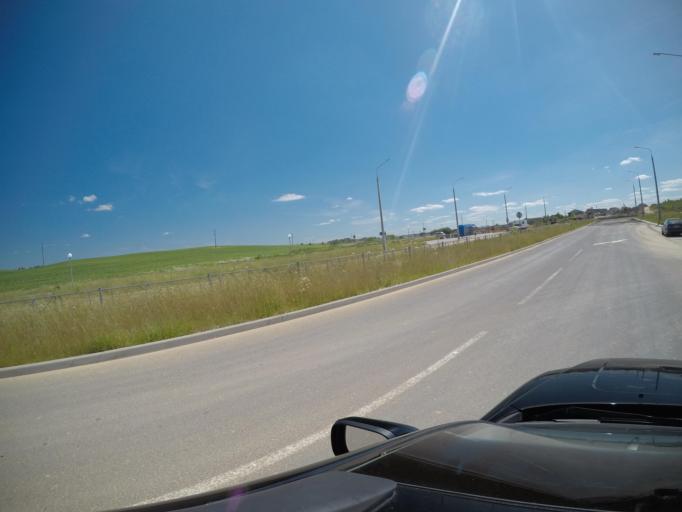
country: BY
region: Grodnenskaya
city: Hrodna
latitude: 53.7219
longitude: 23.8869
